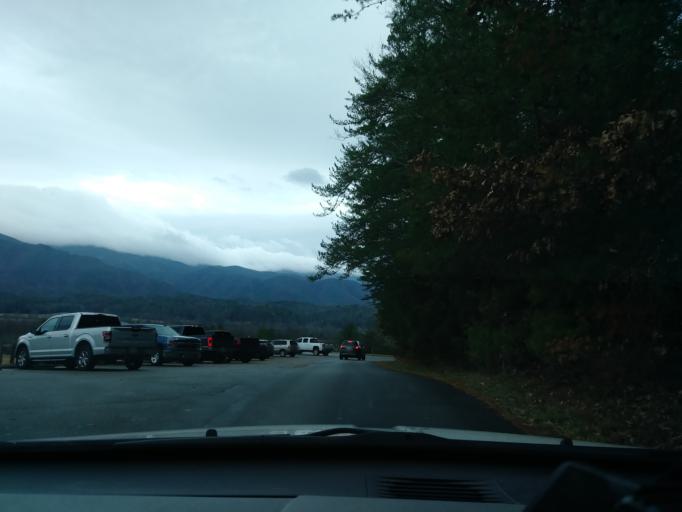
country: US
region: Tennessee
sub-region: Blount County
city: Wildwood
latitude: 35.6061
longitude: -83.8330
